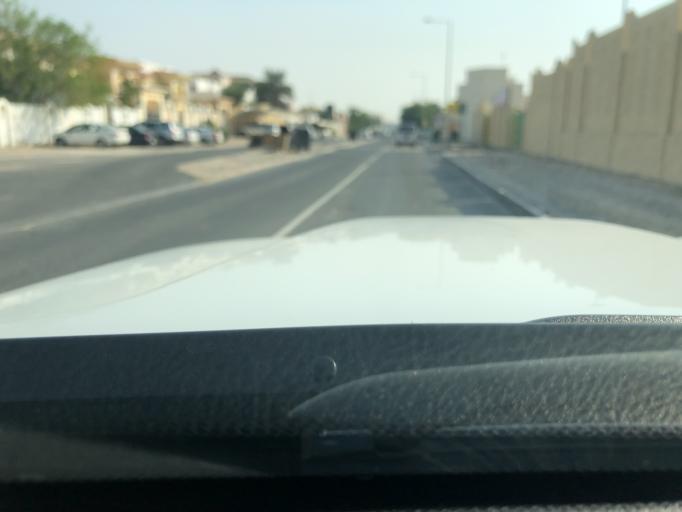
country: QA
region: Baladiyat ar Rayyan
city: Ar Rayyan
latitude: 25.3276
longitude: 51.4744
